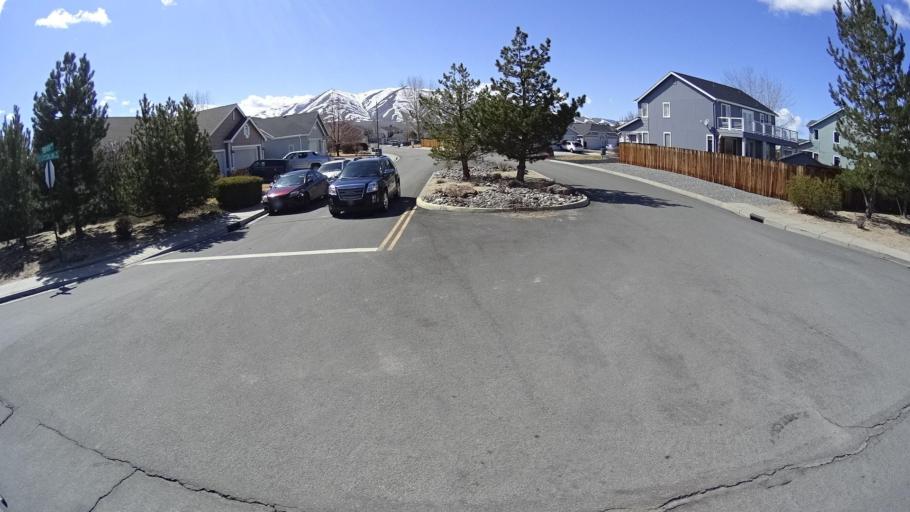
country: US
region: Nevada
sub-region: Washoe County
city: Lemmon Valley
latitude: 39.6358
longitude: -119.8674
